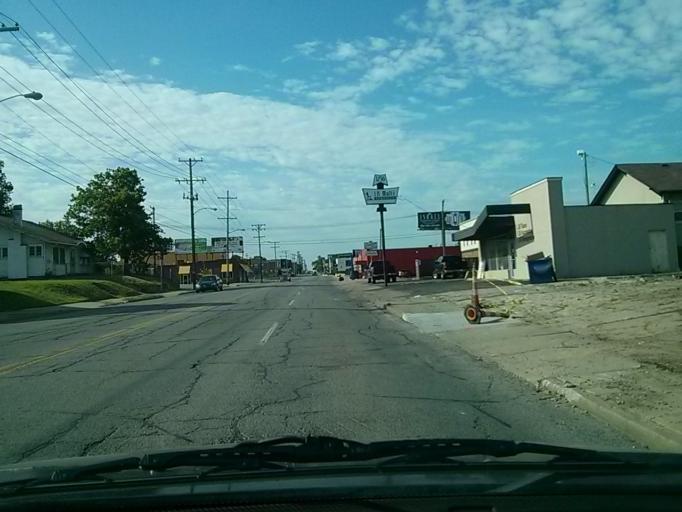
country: US
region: Oklahoma
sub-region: Tulsa County
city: Tulsa
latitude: 36.1452
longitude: -95.9757
